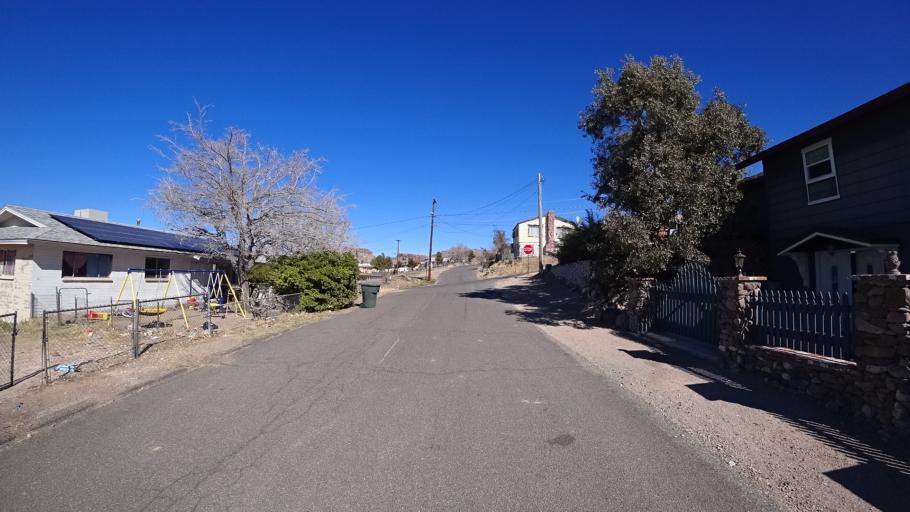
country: US
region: Arizona
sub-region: Mohave County
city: Kingman
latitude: 35.1933
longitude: -114.0624
